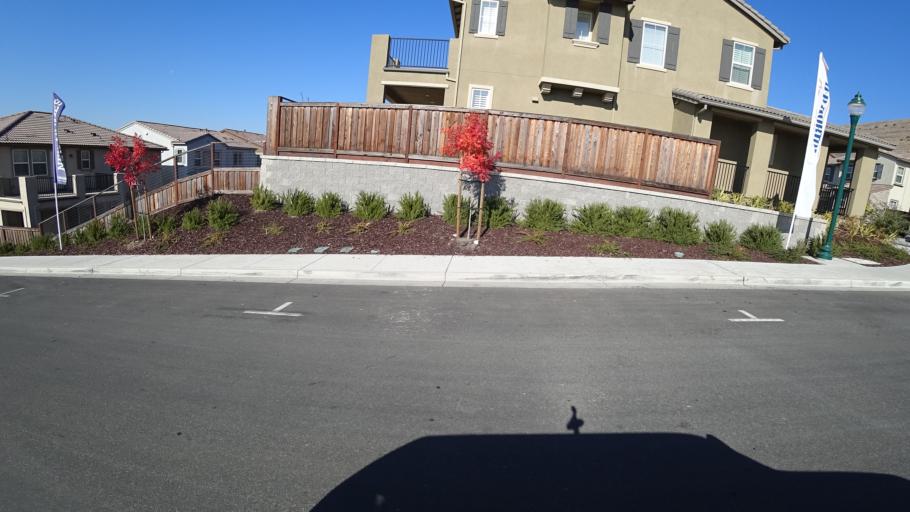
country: US
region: California
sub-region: Alameda County
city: Fairview
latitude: 37.6362
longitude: -122.0446
